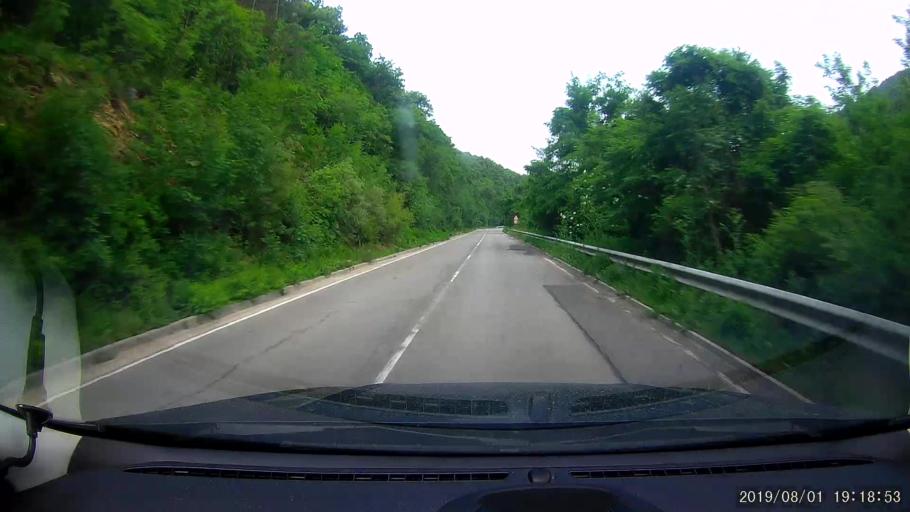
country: BG
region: Shumen
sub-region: Obshtina Smyadovo
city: Smyadovo
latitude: 42.9065
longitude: 26.9405
